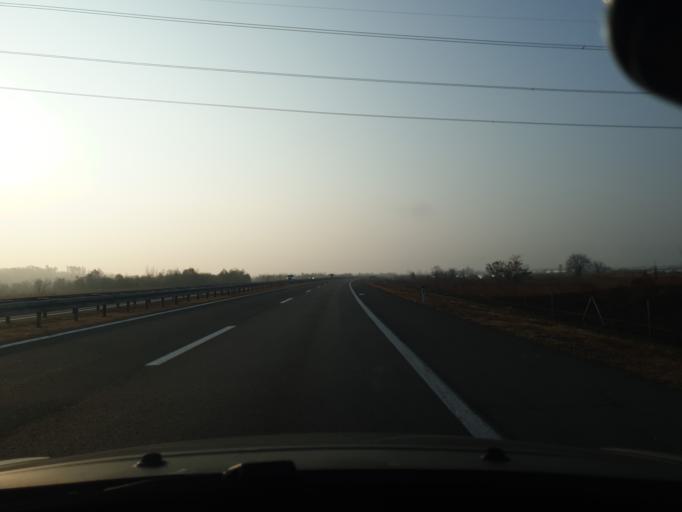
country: RS
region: Central Serbia
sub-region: Jablanicki Okrug
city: Leskovac
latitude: 43.0116
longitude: 22.0236
